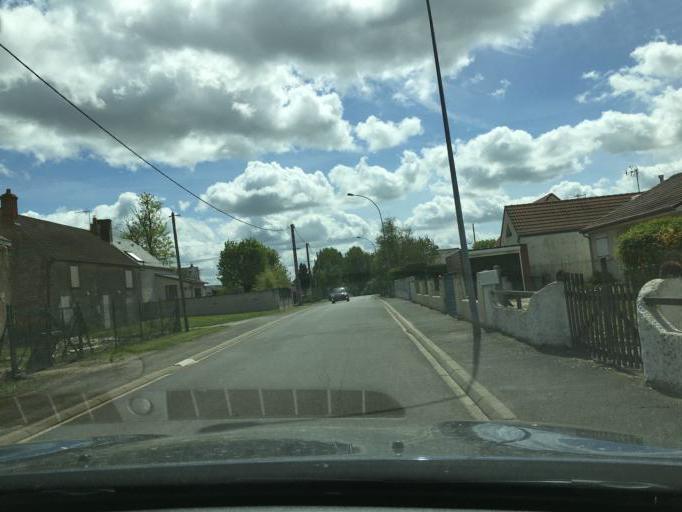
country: FR
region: Centre
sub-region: Departement du Loiret
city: Bricy
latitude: 48.0532
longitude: 1.7982
